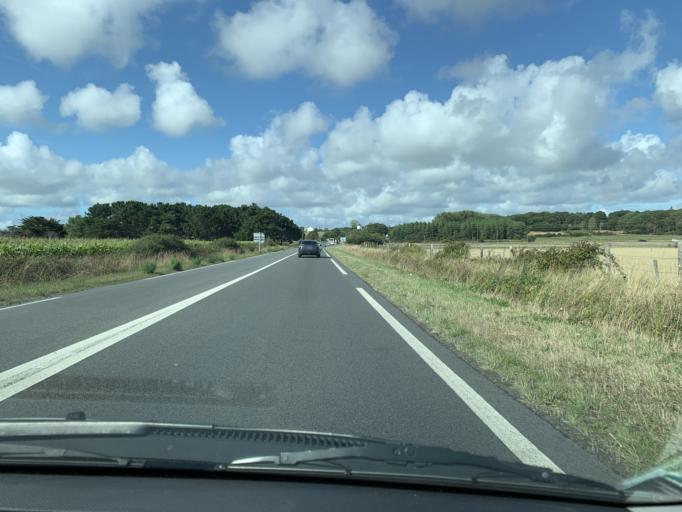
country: FR
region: Pays de la Loire
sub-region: Departement de la Loire-Atlantique
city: Guerande
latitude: 47.3114
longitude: -2.4294
